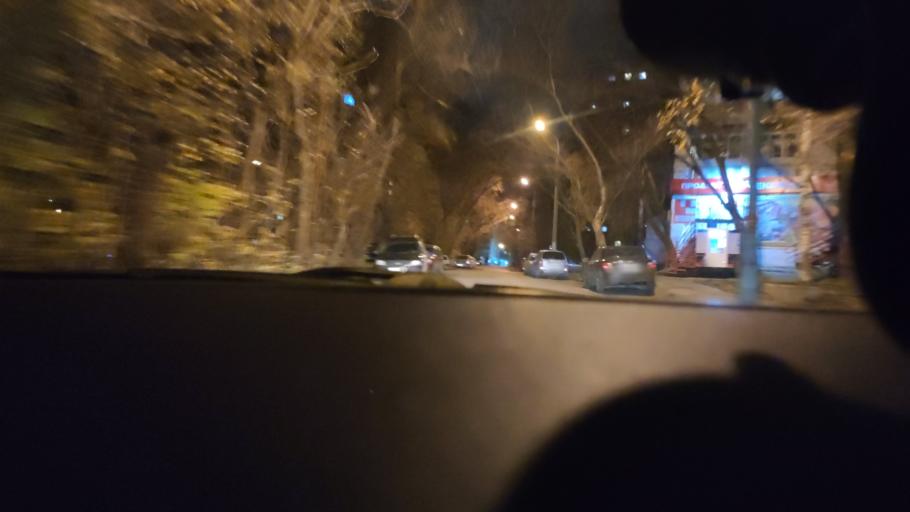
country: RU
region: Perm
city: Perm
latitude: 57.9811
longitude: 56.2322
